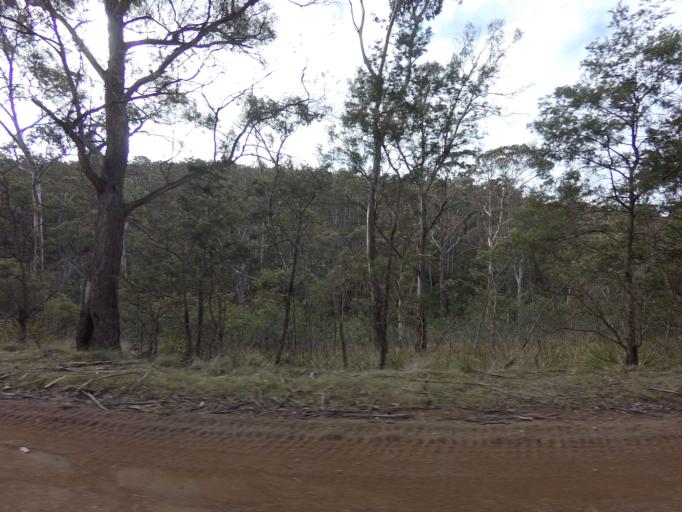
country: AU
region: Tasmania
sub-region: Derwent Valley
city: New Norfolk
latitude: -42.7486
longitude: 146.8694
